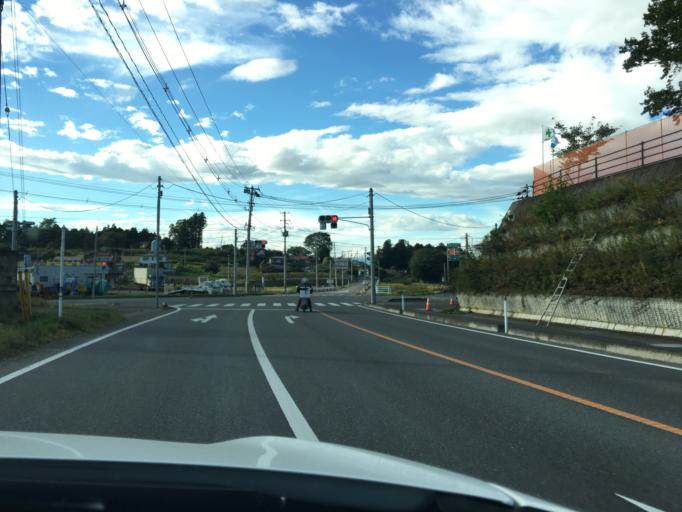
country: JP
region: Fukushima
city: Sukagawa
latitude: 37.2658
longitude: 140.4175
